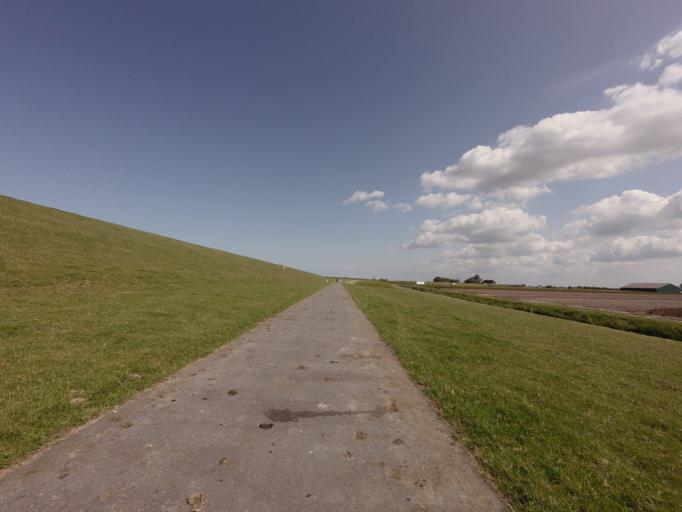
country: NL
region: Friesland
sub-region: Gemeente Dongeradeel
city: Holwerd
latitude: 53.3781
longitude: 5.8839
